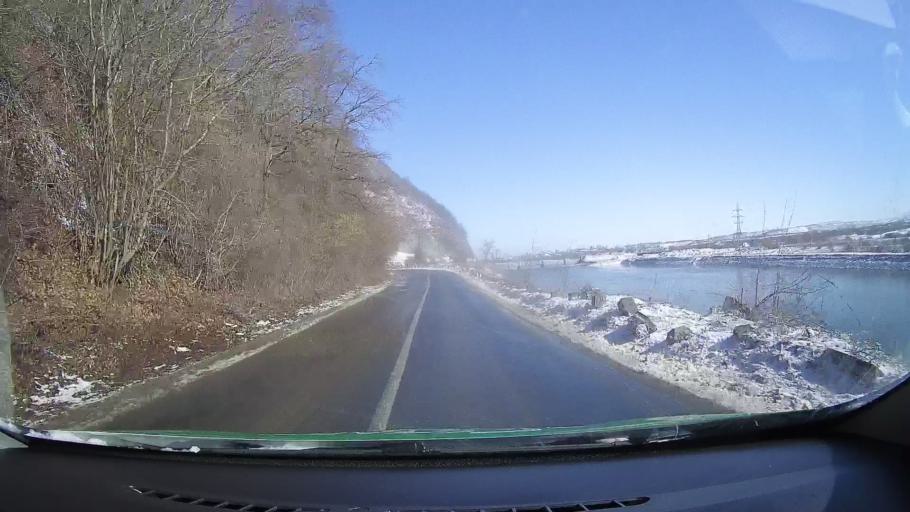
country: RO
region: Sibiu
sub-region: Comuna Turnu Rosu
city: Turnu Rosu
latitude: 45.6658
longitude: 24.3113
